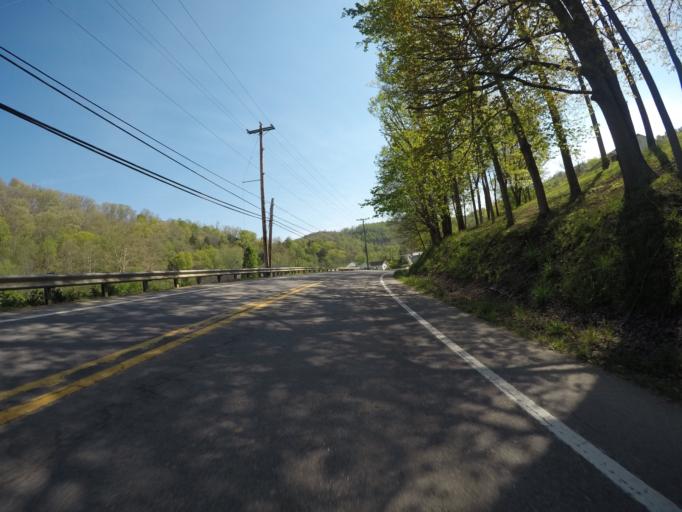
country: US
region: West Virginia
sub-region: Kanawha County
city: Clendenin
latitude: 38.5125
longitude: -81.3566
